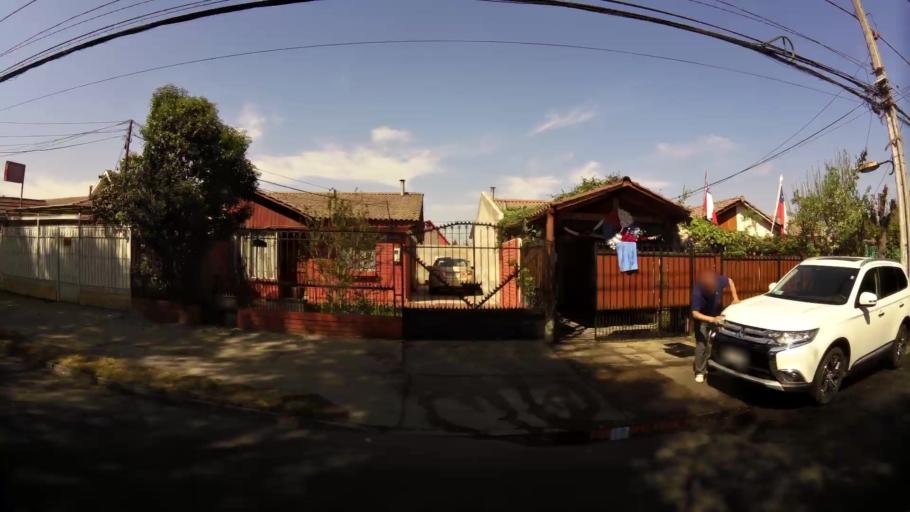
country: CL
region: Santiago Metropolitan
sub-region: Provincia de Santiago
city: Lo Prado
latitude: -33.4703
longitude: -70.7426
